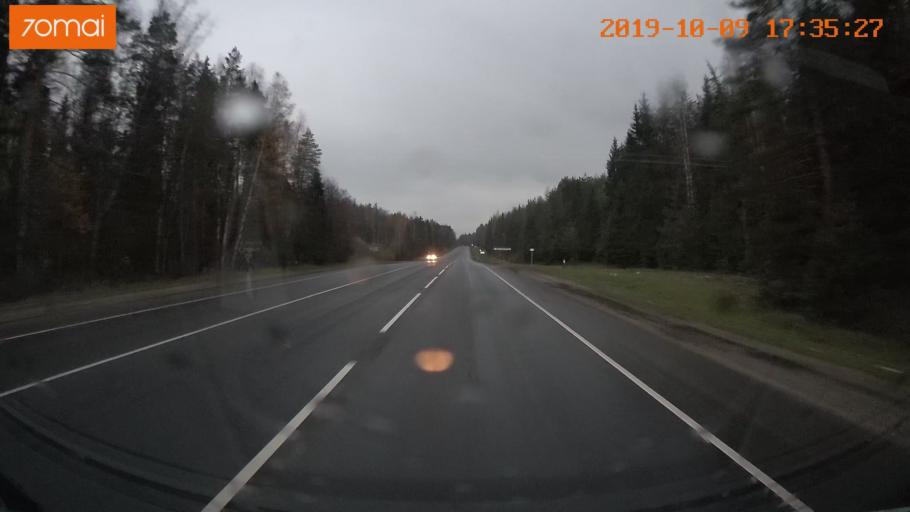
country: RU
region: Ivanovo
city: Bogorodskoye
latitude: 57.0936
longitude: 41.0022
